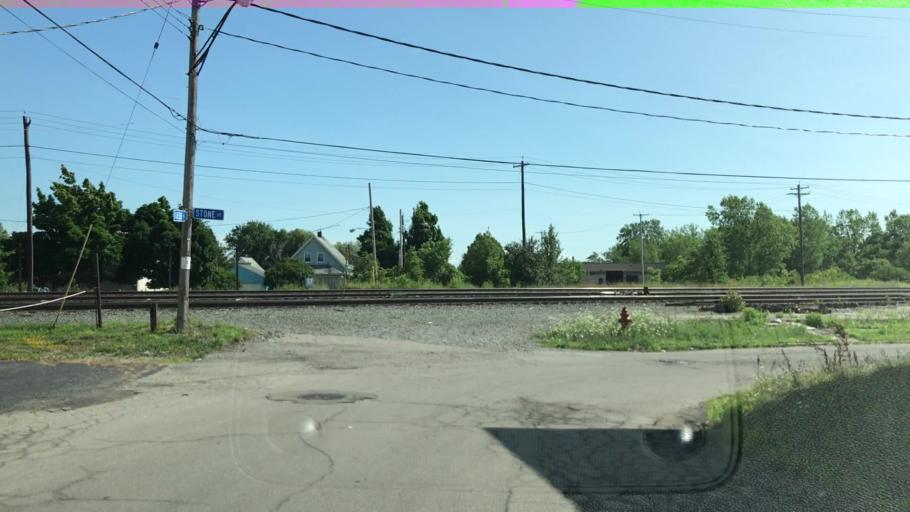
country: US
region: New York
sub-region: Erie County
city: Sloan
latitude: 42.8967
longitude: -78.8095
